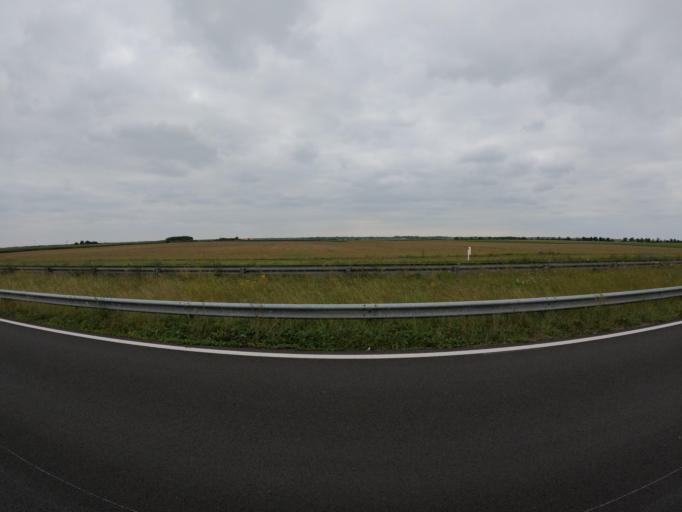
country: FR
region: Pays de la Loire
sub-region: Departement de la Vendee
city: Maillezais
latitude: 46.4247
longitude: -0.7166
